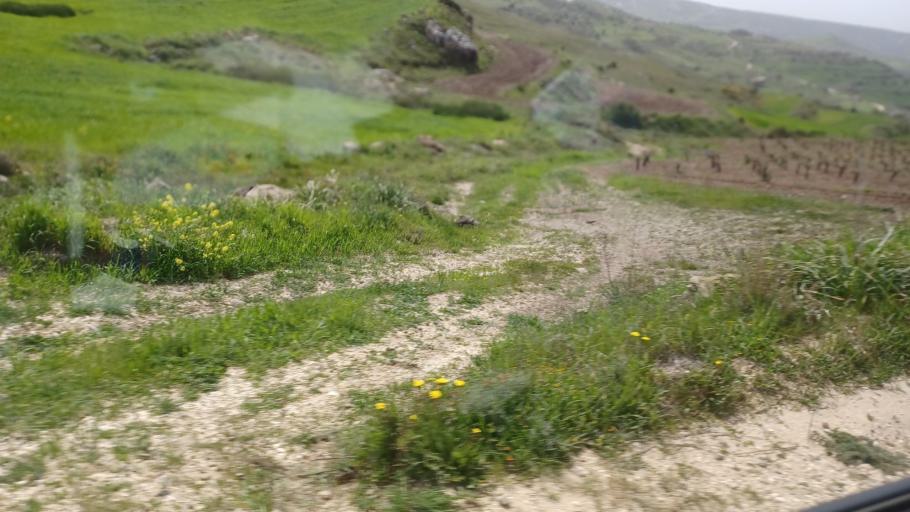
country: CY
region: Pafos
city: Polis
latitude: 34.9760
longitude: 32.3630
